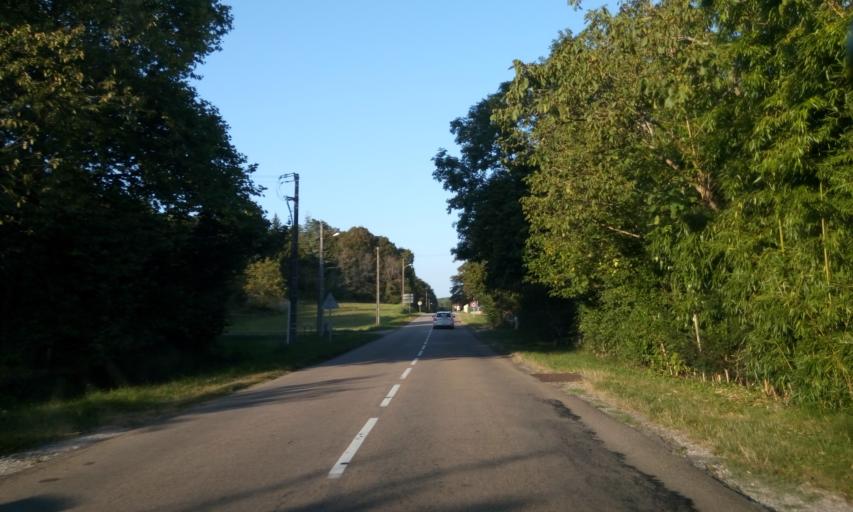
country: FR
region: Rhone-Alpes
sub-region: Departement de l'Ain
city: Priay
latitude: 46.0352
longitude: 5.3111
